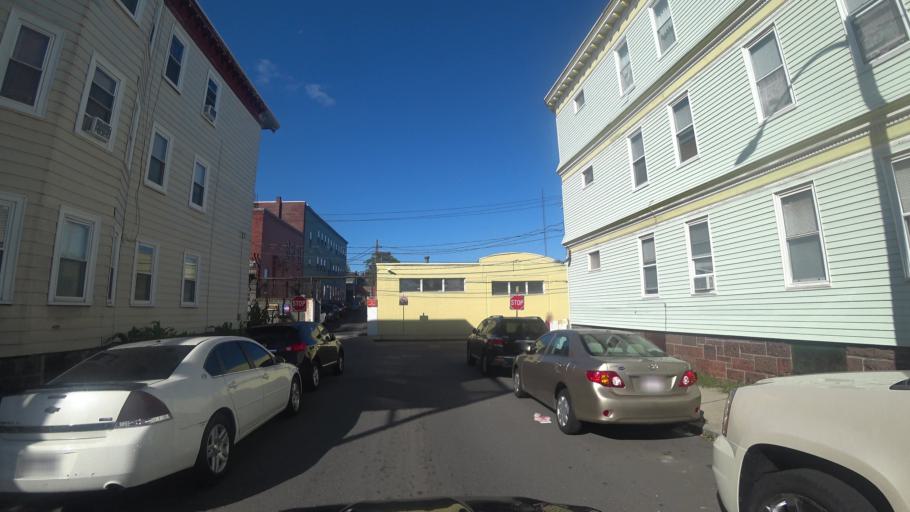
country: US
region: Massachusetts
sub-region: Suffolk County
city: South Boston
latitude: 42.3205
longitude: -71.0652
